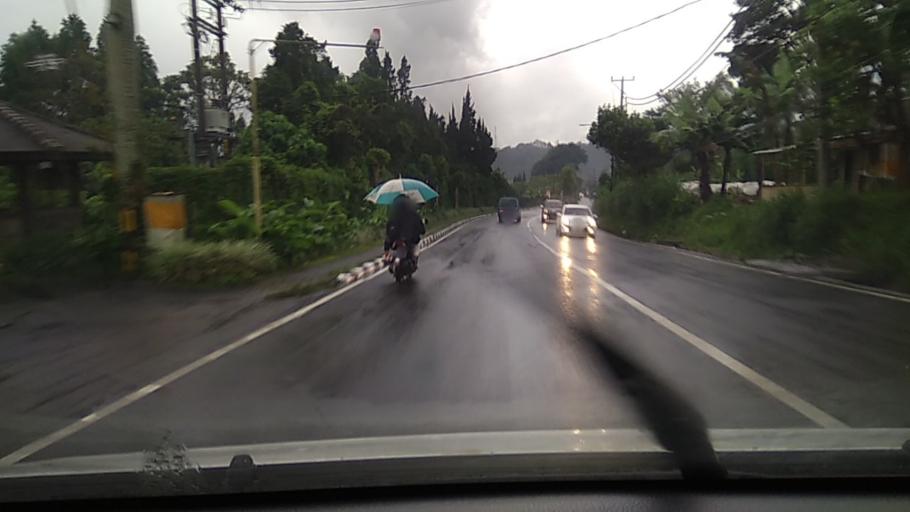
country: ID
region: Bali
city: Munduk
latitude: -8.2658
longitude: 115.1645
